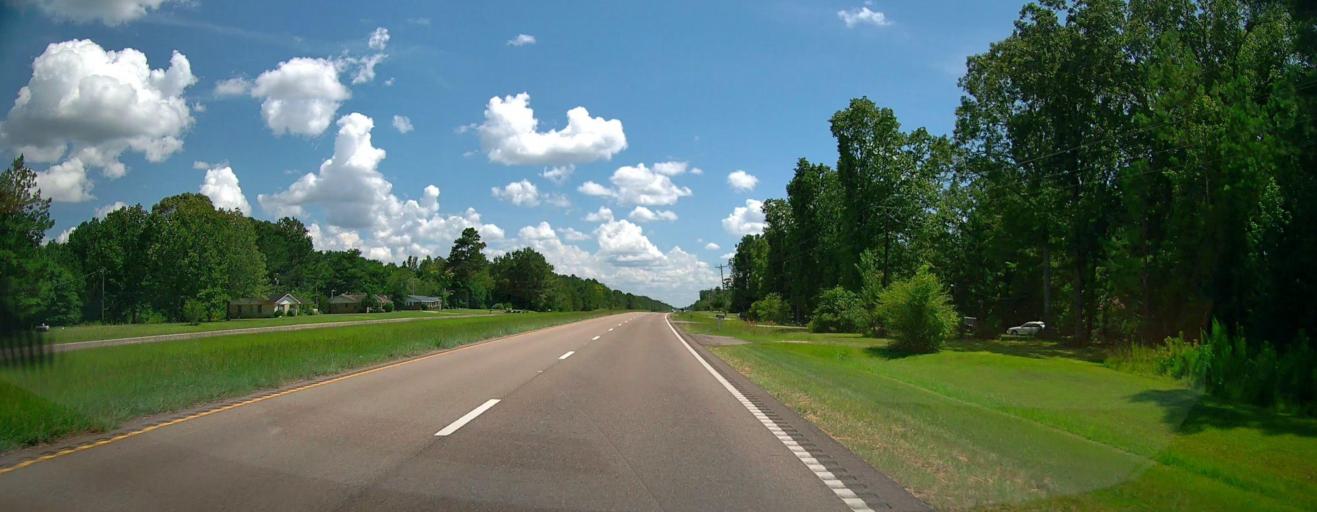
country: US
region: Mississippi
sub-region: Monroe County
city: Aberdeen
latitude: 33.9285
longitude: -88.5963
